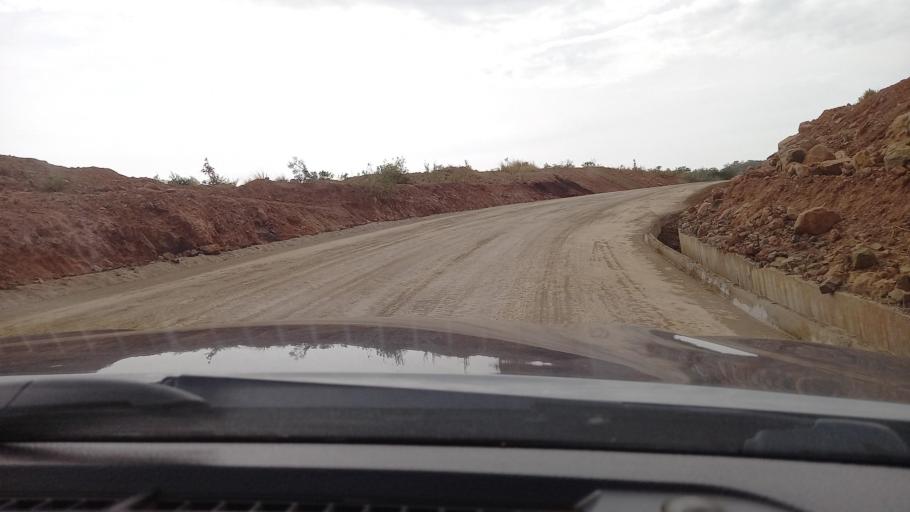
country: ET
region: Southern Nations, Nationalities, and People's Region
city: Mizan Teferi
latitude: 6.1921
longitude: 35.6857
